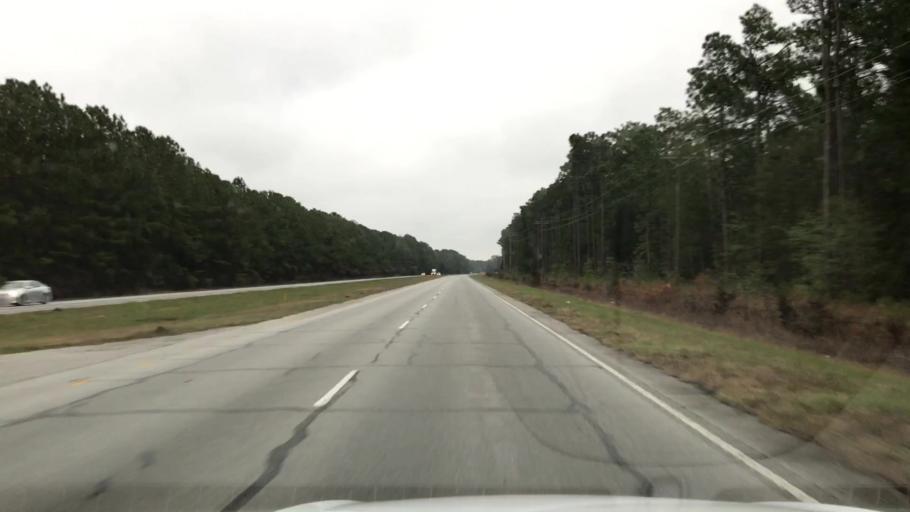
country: US
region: South Carolina
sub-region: Charleston County
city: Awendaw
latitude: 33.0686
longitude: -79.5242
